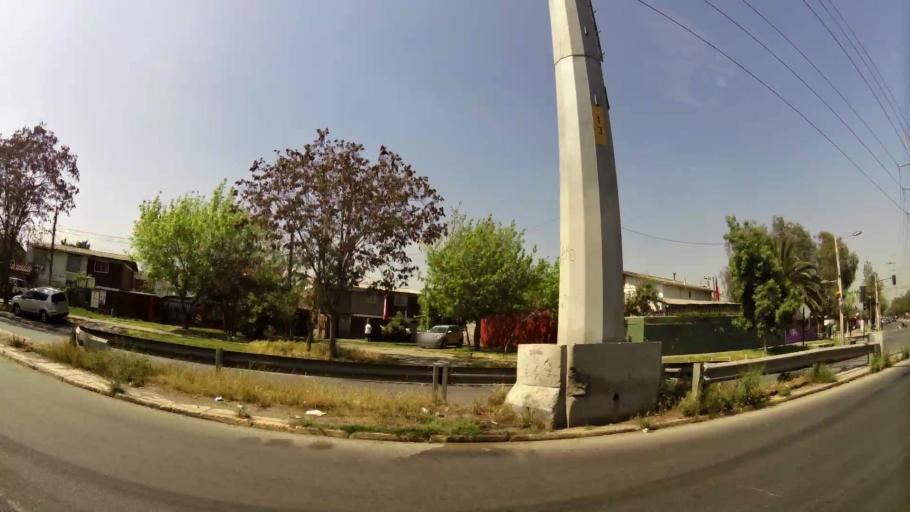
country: CL
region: Santiago Metropolitan
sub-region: Provincia de Santiago
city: La Pintana
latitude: -33.5583
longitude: -70.6011
